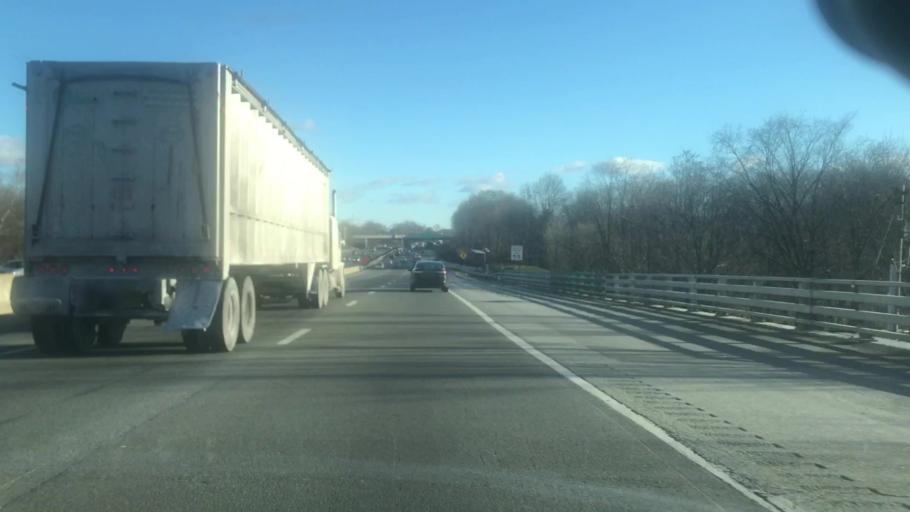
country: US
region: New York
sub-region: Rockland County
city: Spring Valley
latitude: 41.0999
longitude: -74.0333
